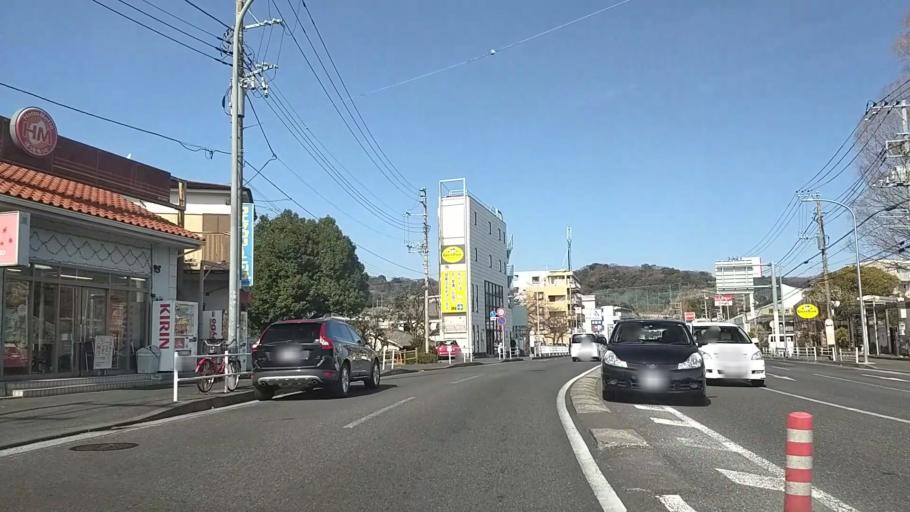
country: JP
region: Kanagawa
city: Zushi
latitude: 35.3448
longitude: 139.6108
